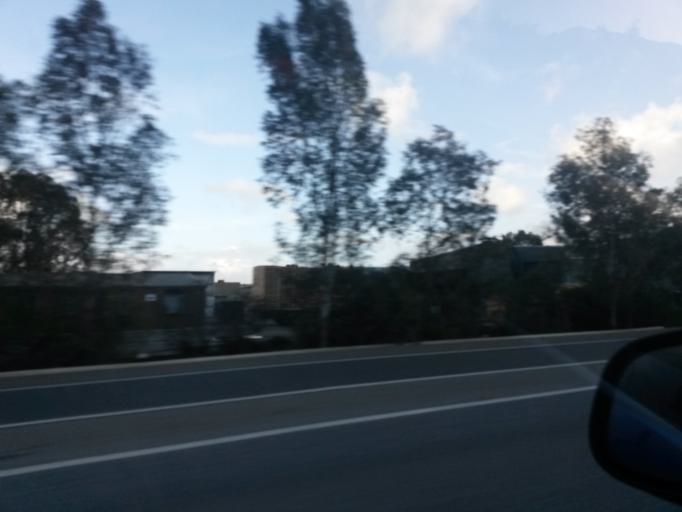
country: AU
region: South Australia
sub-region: Charles Sturt
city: Woodville North
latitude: -34.8331
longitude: 138.5600
